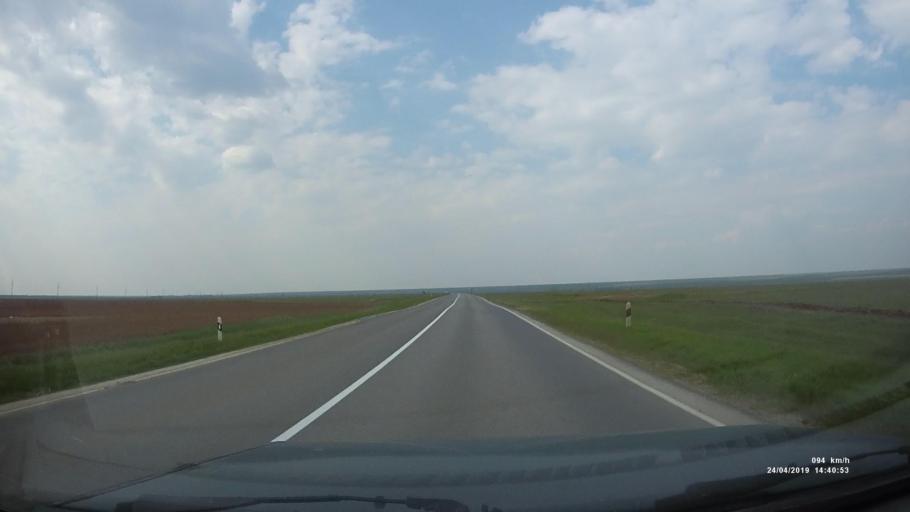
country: RU
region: Rostov
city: Remontnoye
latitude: 46.4385
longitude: 43.8849
